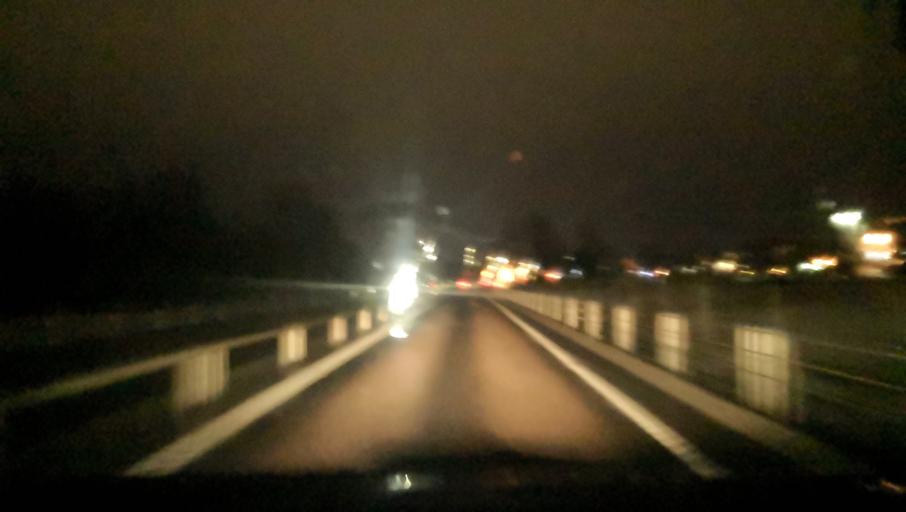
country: SE
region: Uppsala
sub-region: Enkopings Kommun
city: Enkoping
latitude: 59.6610
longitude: 17.0757
